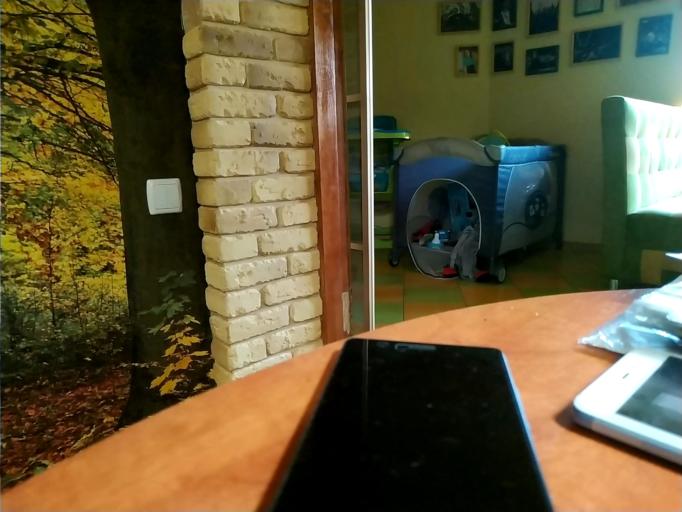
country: RU
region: Kaluga
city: Seredeyskiy
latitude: 53.7723
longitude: 35.4039
